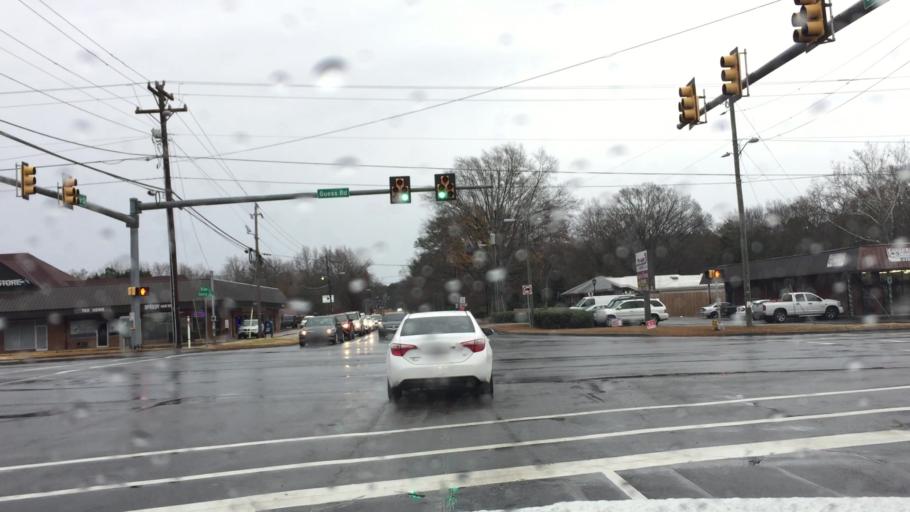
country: US
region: North Carolina
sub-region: Durham County
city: Durham
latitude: 36.0378
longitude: -78.9298
